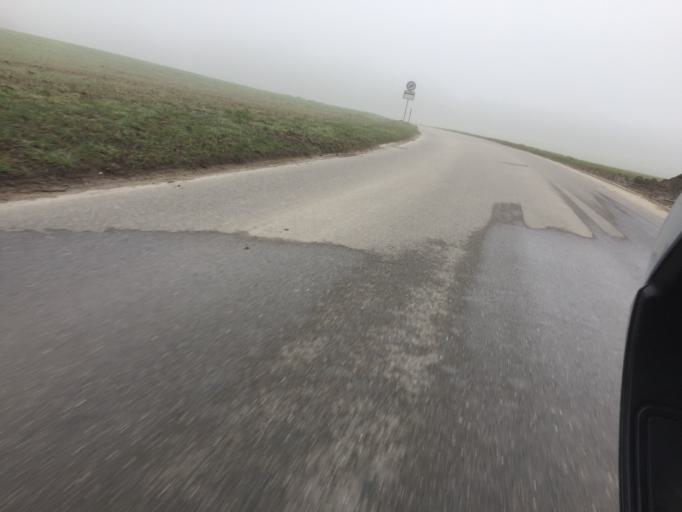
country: CH
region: Bern
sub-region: Seeland District
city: Grossaffoltern
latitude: 47.0986
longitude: 7.3640
